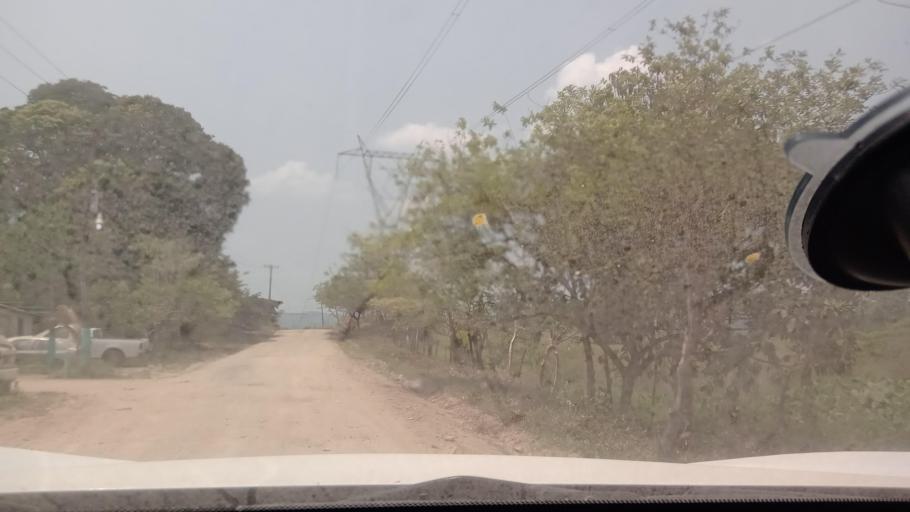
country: MX
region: Chiapas
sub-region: Tecpatan
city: Raudales Malpaso
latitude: 17.4534
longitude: -93.7935
